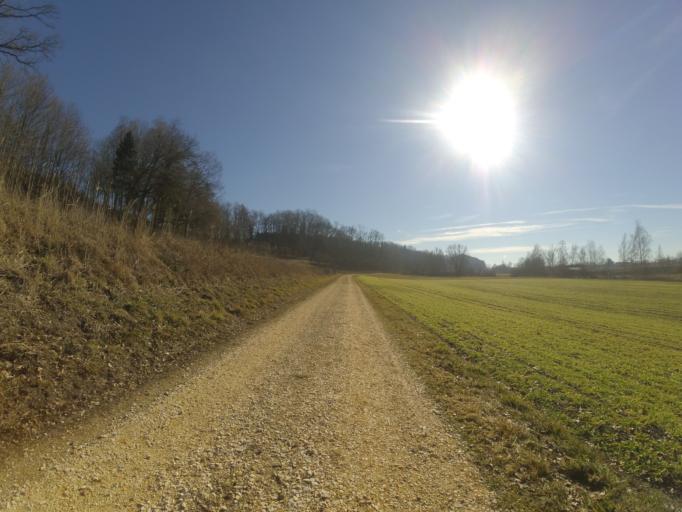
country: DE
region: Baden-Wuerttemberg
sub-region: Tuebingen Region
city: Huttisheim
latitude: 48.2909
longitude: 9.9374
